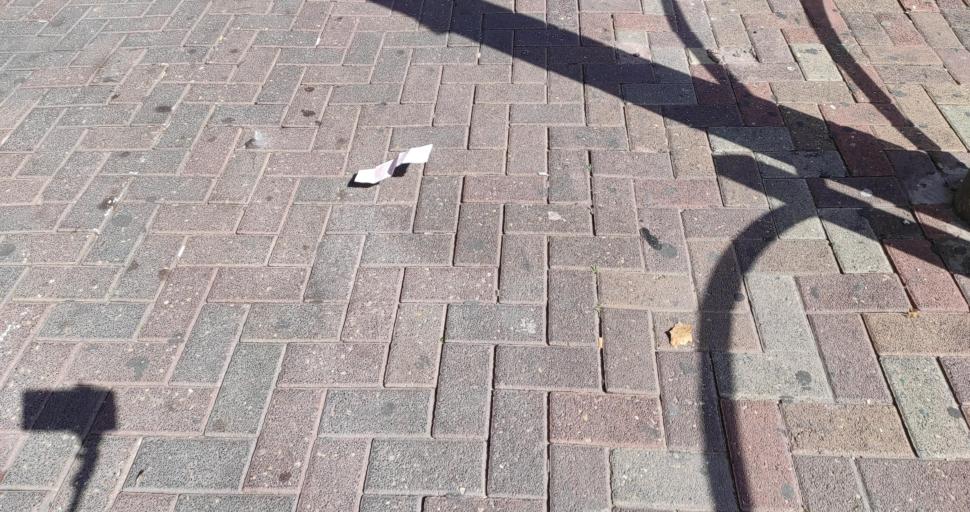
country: IL
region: Central District
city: Netanya
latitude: 32.3282
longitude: 34.8586
